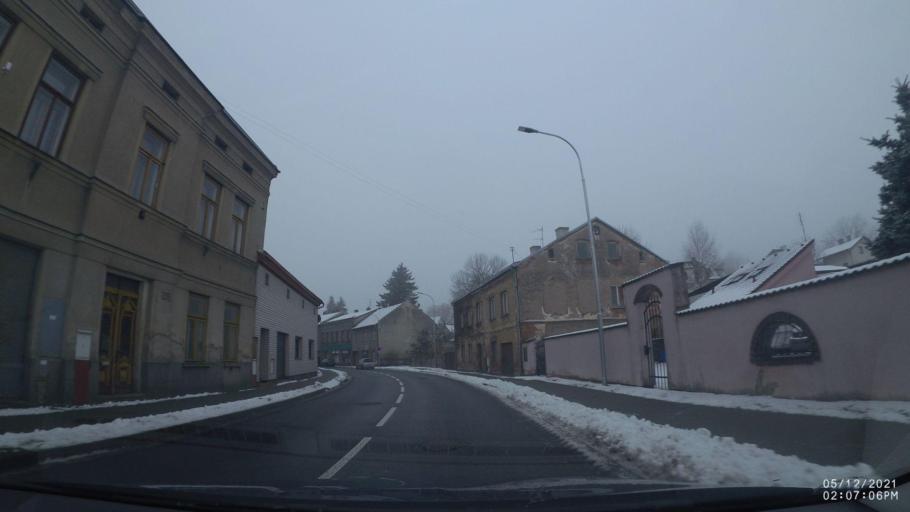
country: CZ
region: Kralovehradecky
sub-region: Okres Nachod
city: Cerveny Kostelec
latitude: 50.4799
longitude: 16.0979
